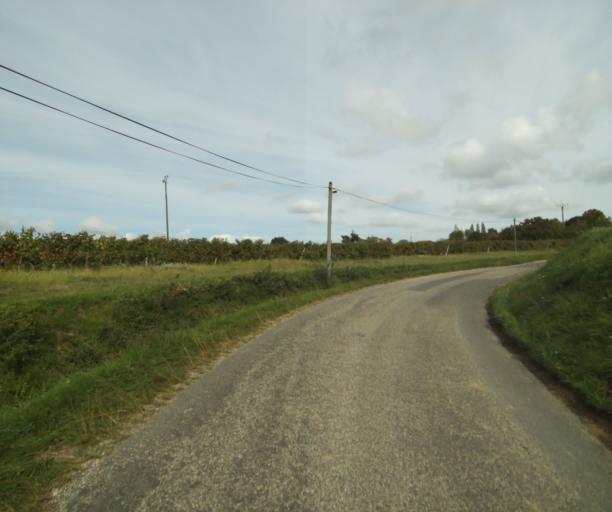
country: FR
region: Midi-Pyrenees
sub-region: Departement du Gers
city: Eauze
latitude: 43.8426
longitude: 0.1412
